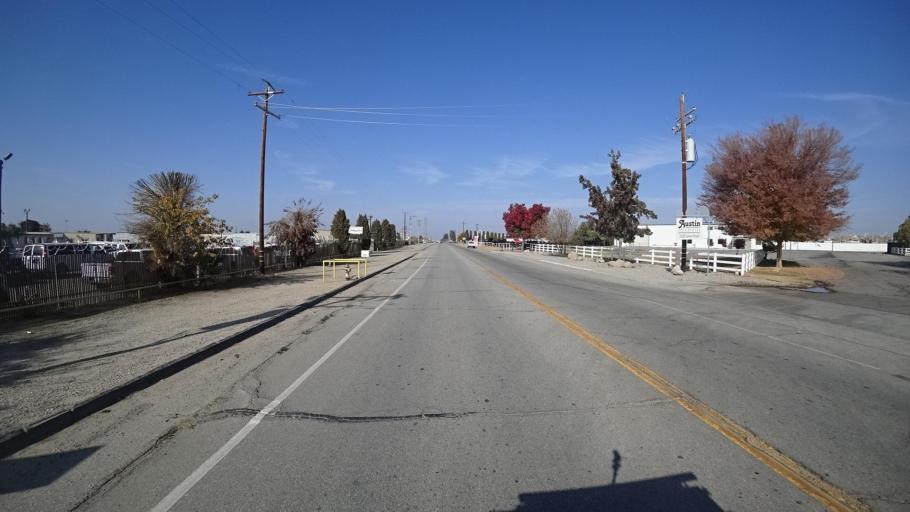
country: US
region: California
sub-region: Kern County
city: Oildale
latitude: 35.4497
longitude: -119.0328
